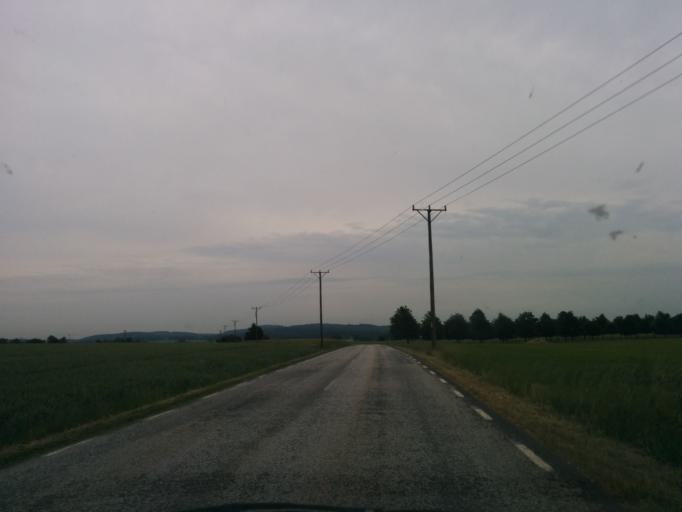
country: SE
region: Skane
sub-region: Lunds Kommun
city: Genarp
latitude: 55.6400
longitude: 13.3598
